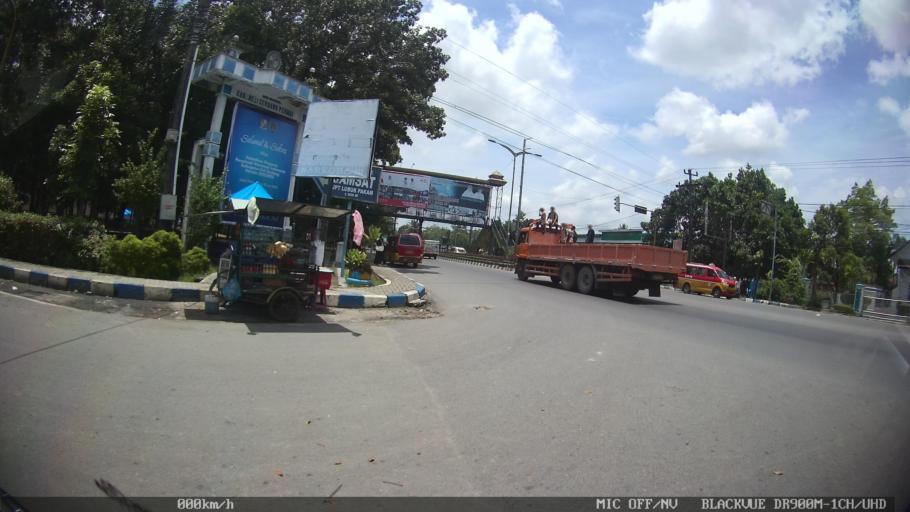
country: ID
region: North Sumatra
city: Percut
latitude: 3.5516
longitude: 98.8655
